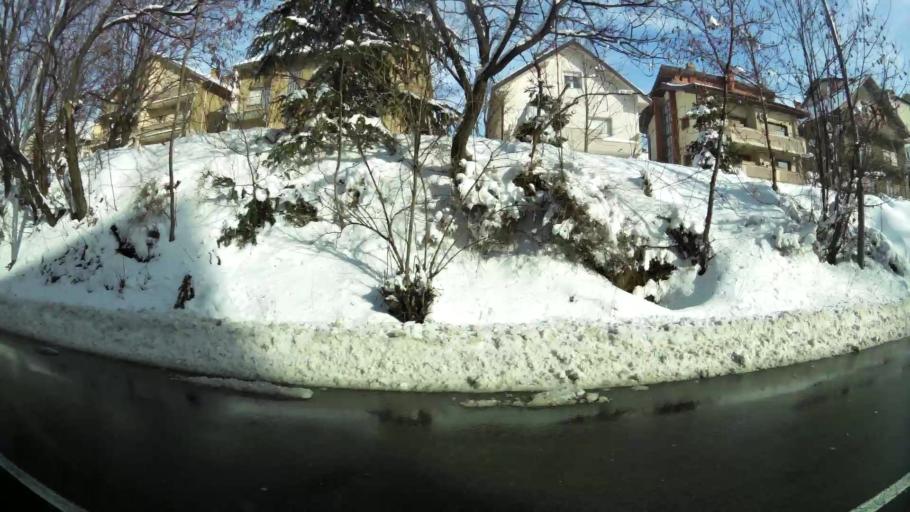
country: RS
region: Central Serbia
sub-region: Belgrade
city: Zvezdara
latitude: 44.7924
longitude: 20.5322
